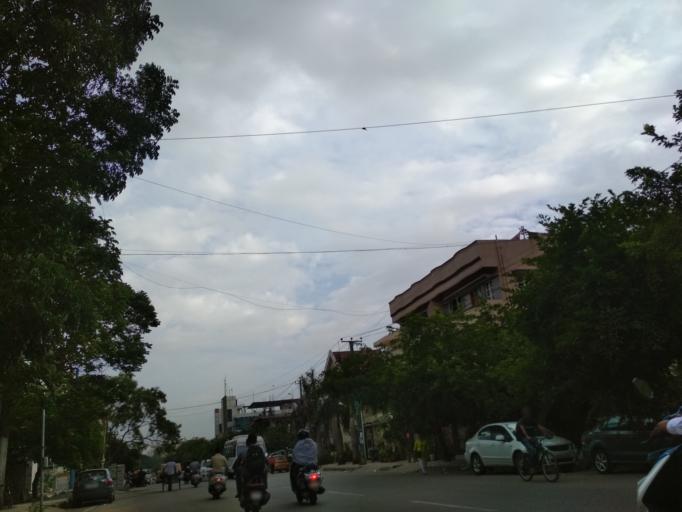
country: IN
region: Karnataka
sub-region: Bangalore Urban
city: Bangalore
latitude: 12.9185
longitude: 77.6450
